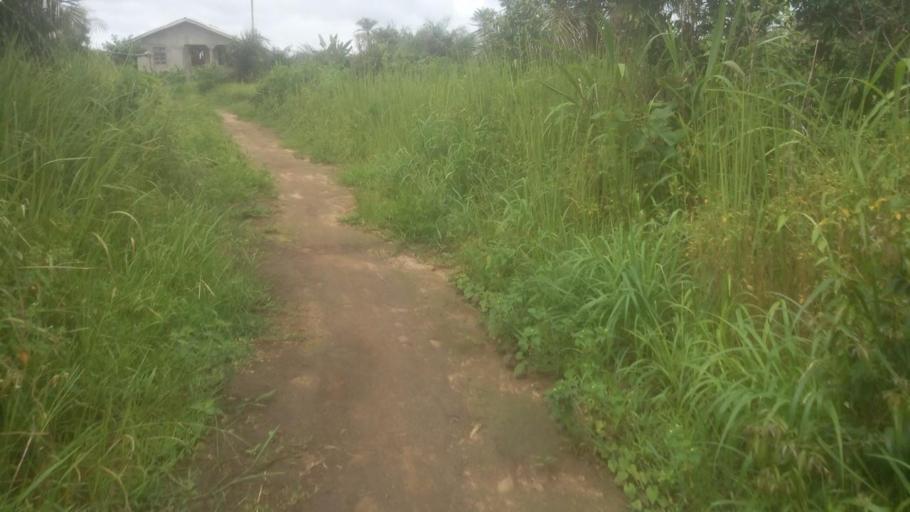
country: SL
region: Northern Province
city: Masoyila
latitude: 8.5895
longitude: -13.1843
